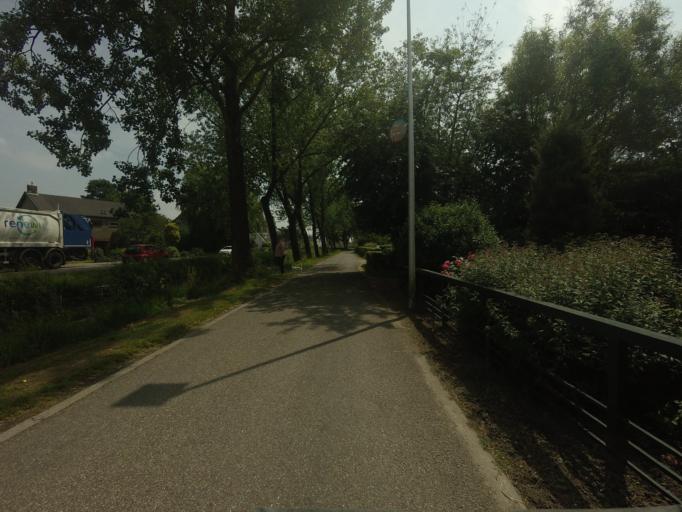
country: NL
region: Utrecht
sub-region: Gemeente Houten
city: Houten
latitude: 51.9936
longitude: 5.1868
